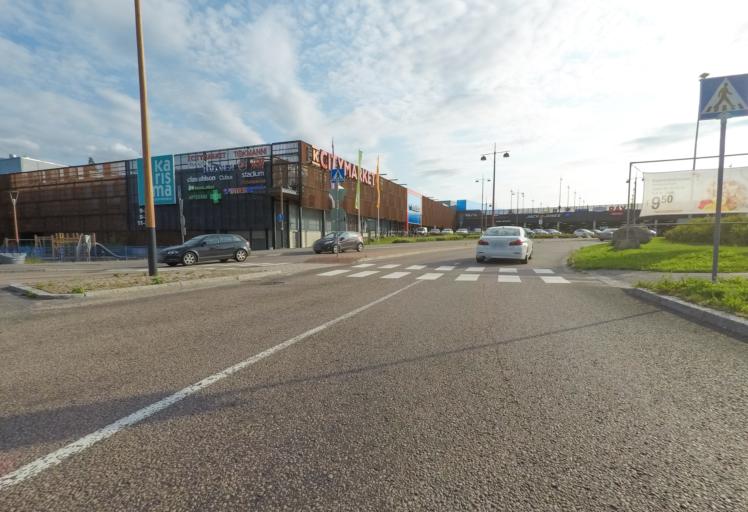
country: FI
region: Paijanne Tavastia
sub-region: Lahti
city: Lahti
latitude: 60.9832
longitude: 25.7383
